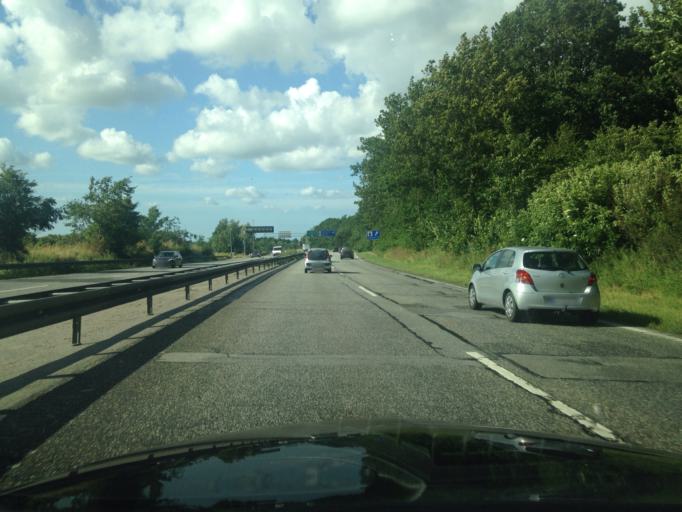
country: DK
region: Capital Region
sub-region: Horsholm Kommune
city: Horsholm
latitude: 55.8710
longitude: 12.4827
